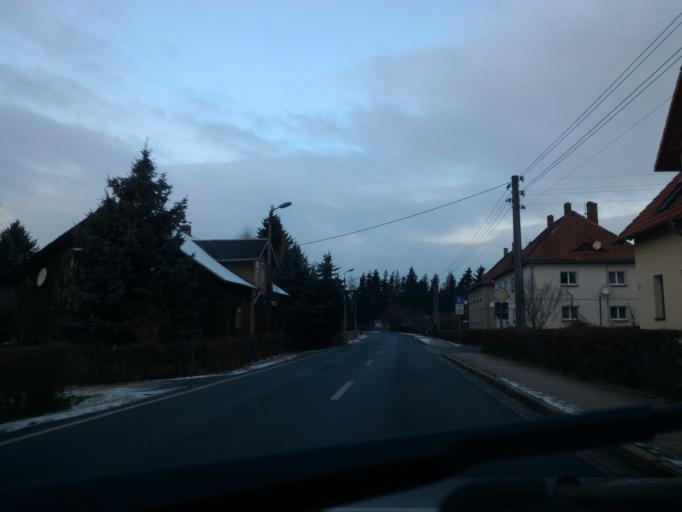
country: DE
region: Saxony
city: Leutersdorf
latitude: 50.9521
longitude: 14.6616
